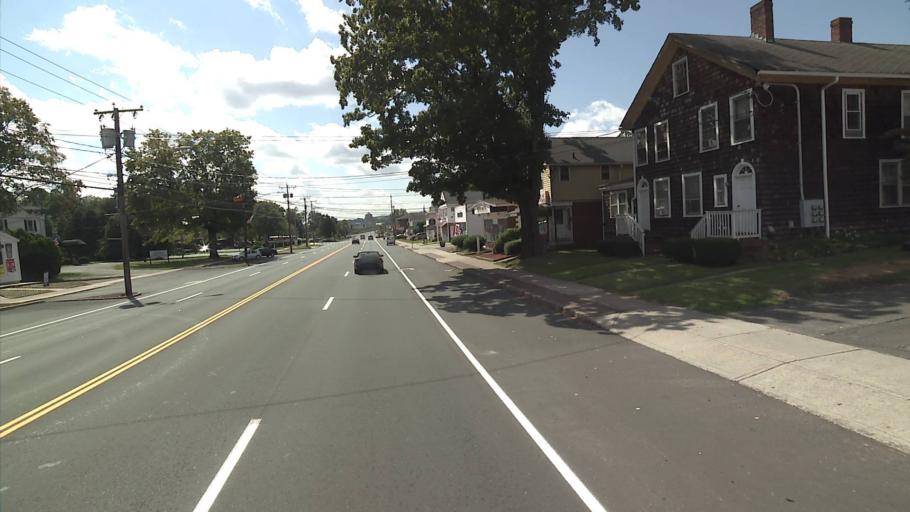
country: US
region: Connecticut
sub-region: Middlesex County
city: Portland
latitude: 41.5745
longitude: -72.6397
